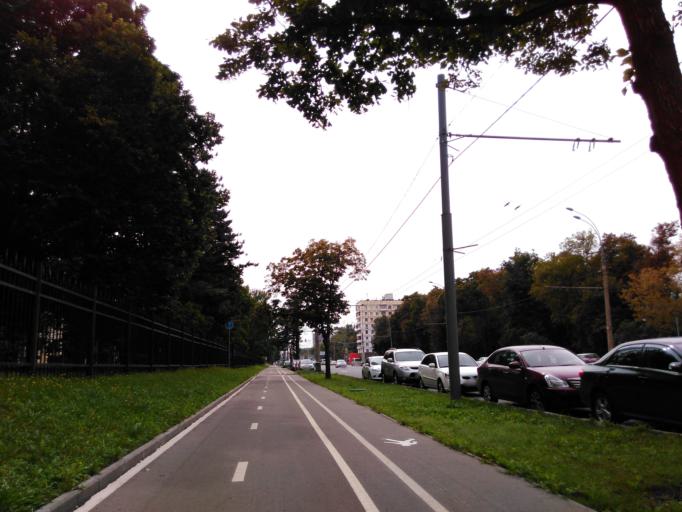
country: RU
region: Moscow
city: Vorob'yovo
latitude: 55.7227
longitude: 37.5283
